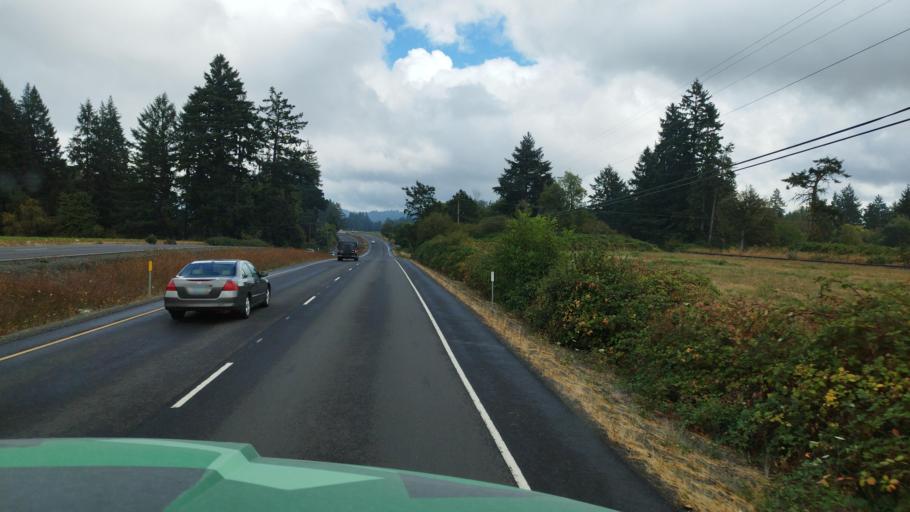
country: US
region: Oregon
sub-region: Yamhill County
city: Lafayette
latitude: 45.2410
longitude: -123.1373
